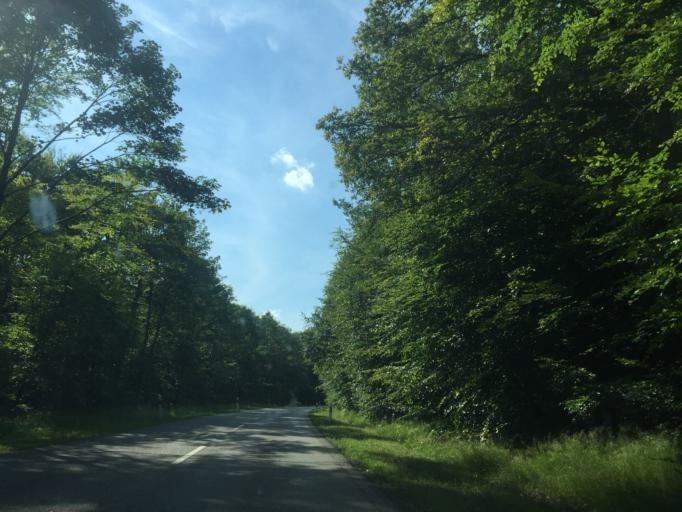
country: DE
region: Baden-Wuerttemberg
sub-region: Karlsruhe Region
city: Gaiberg
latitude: 49.3713
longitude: 8.7345
